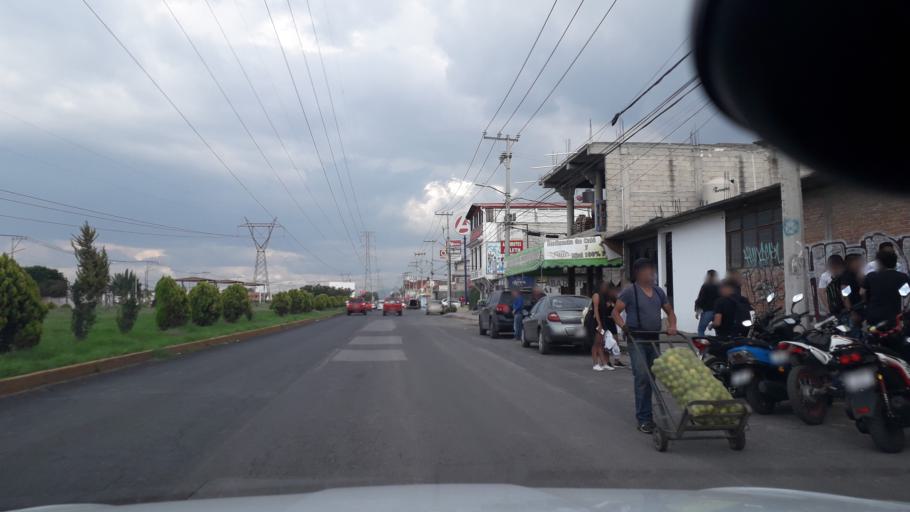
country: MX
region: Mexico
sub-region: Tultitlan
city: Fuentes del Valle
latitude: 19.6407
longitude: -99.1299
